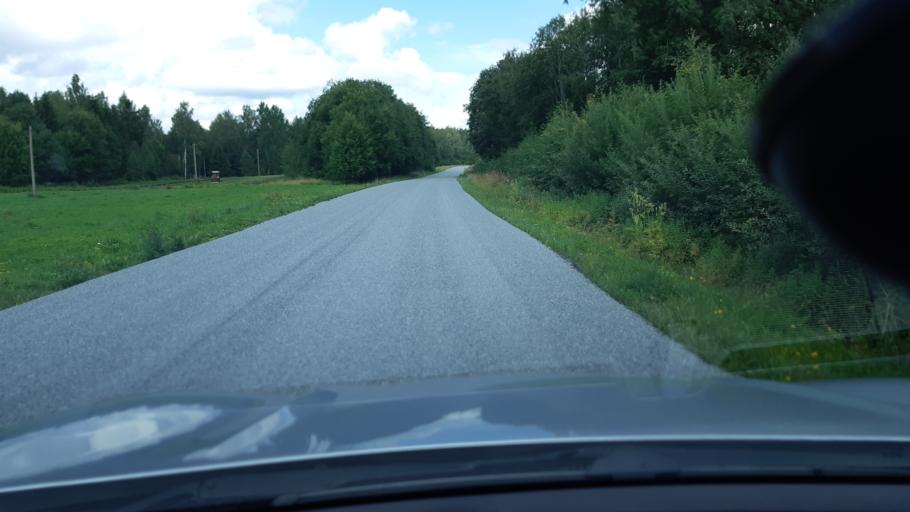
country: EE
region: Raplamaa
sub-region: Kehtna vald
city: Kehtna
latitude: 58.8978
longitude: 25.0270
